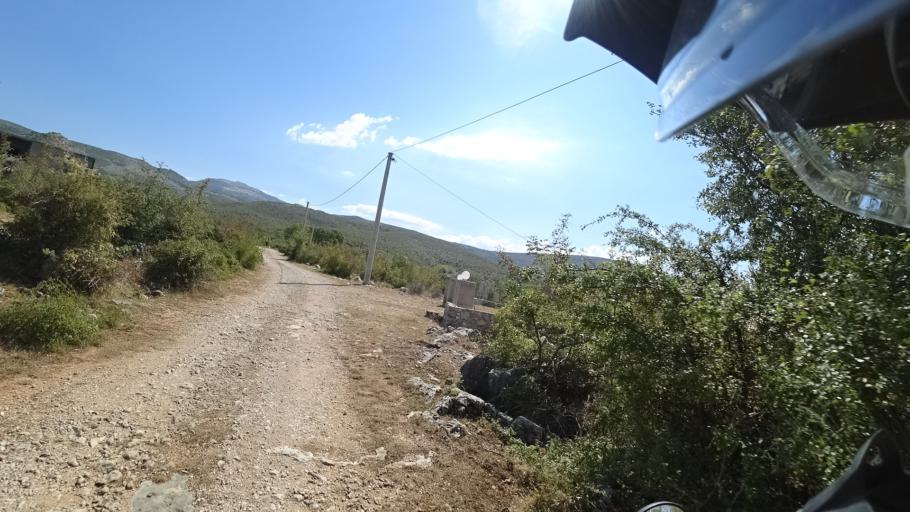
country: HR
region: Sibensko-Kniniska
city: Drnis
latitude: 43.8115
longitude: 16.3402
